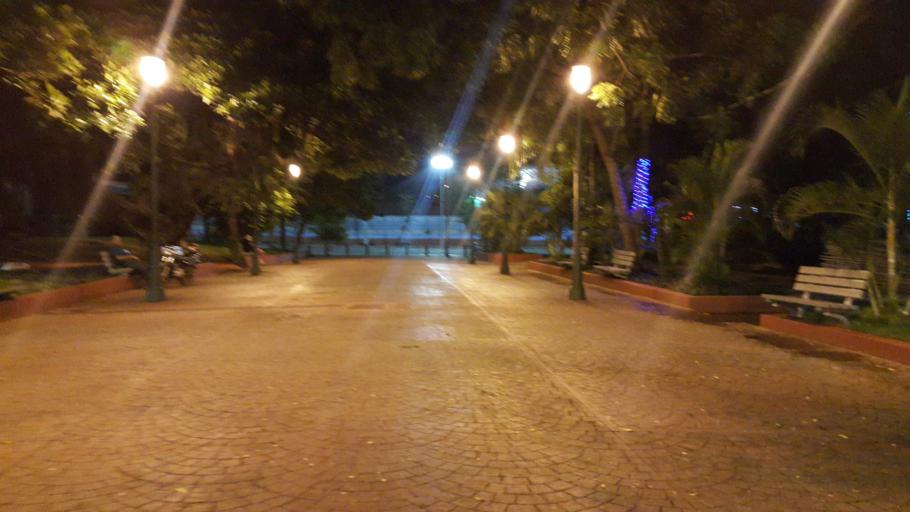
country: NI
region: Managua
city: Managua
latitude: 12.1559
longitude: -86.2729
